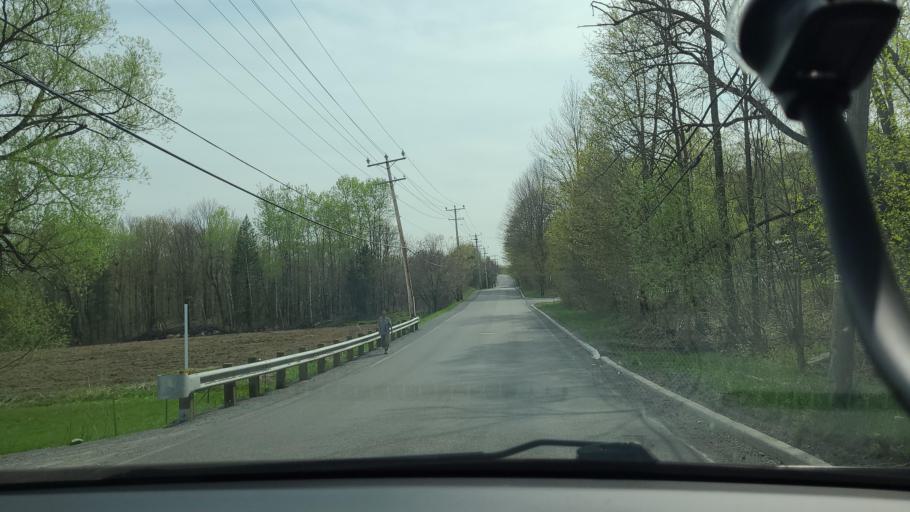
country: CA
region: Quebec
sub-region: Laurentides
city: Prevost
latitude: 45.8810
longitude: -74.0610
